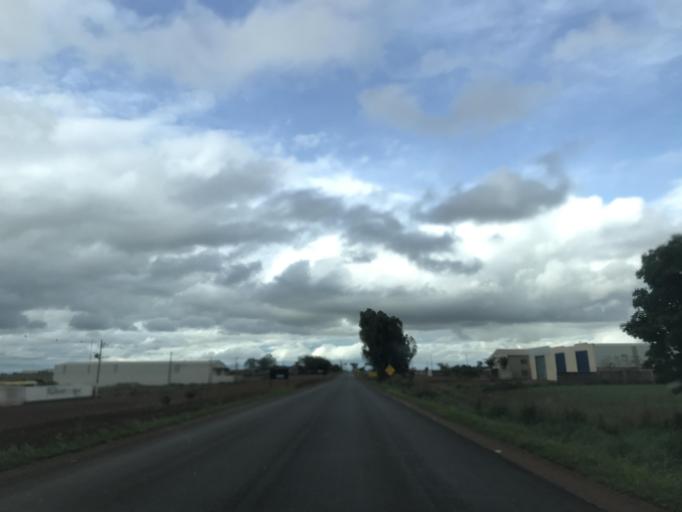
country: BR
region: Goias
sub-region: Vianopolis
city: Vianopolis
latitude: -16.7698
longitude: -48.5225
